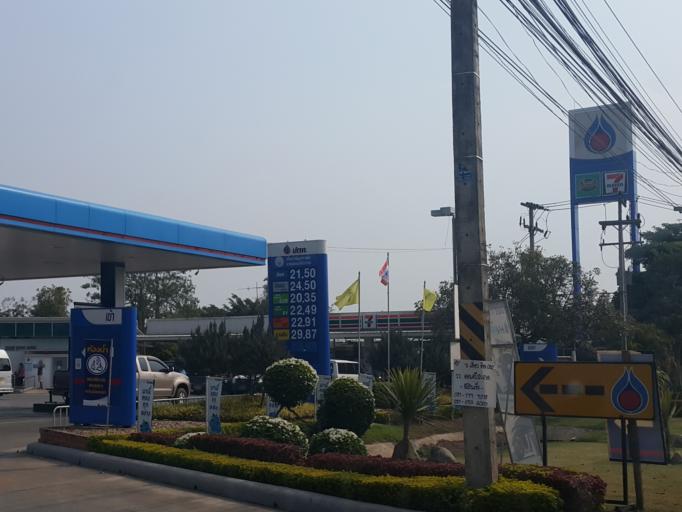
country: TH
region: Chiang Mai
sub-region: Amphoe Chiang Dao
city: Chiang Dao
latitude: 19.3536
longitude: 98.9635
